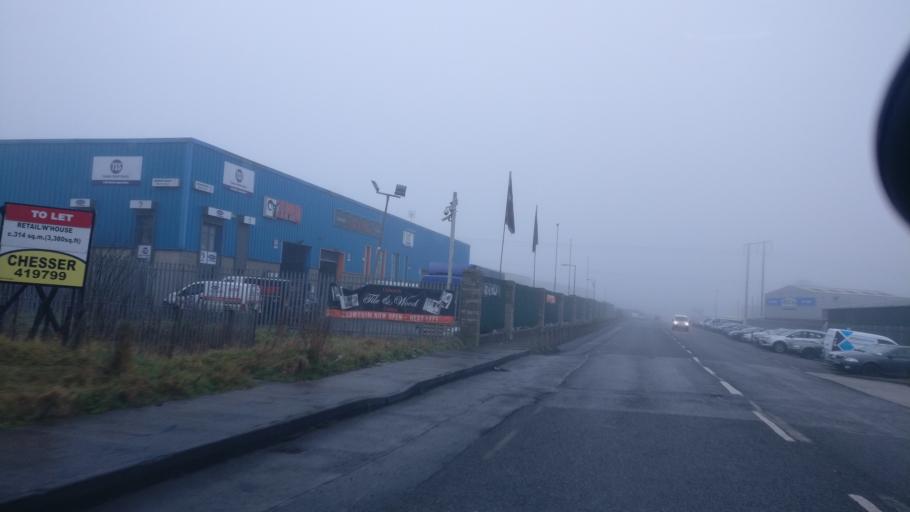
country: IE
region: Munster
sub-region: County Limerick
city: Annacotty
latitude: 52.6491
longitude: -8.5824
